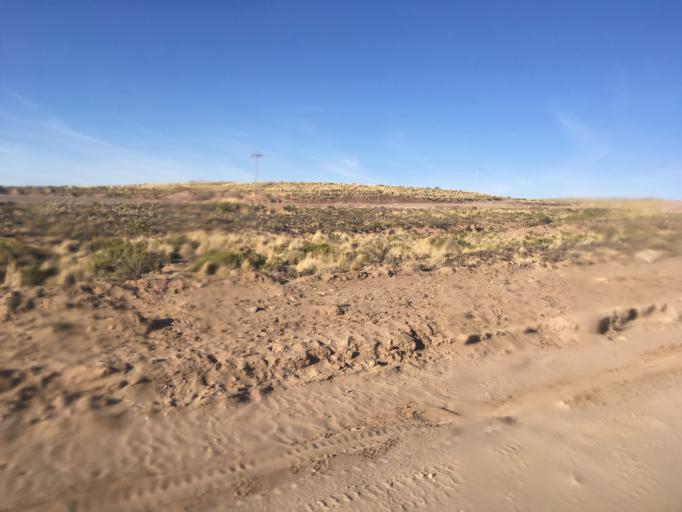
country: PE
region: Puno
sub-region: Provincia de Chucuito
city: Kelluyo
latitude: -16.9762
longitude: -69.0218
